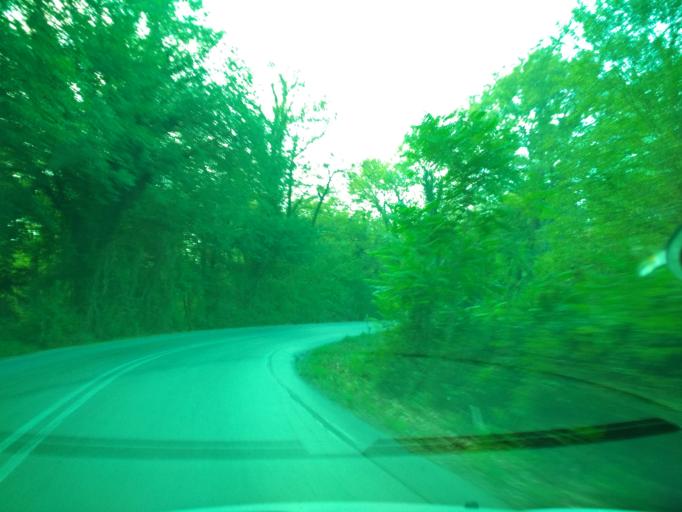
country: GR
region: Central Greece
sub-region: Nomos Evvoias
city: Prokopion
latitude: 38.7496
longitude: 23.4872
